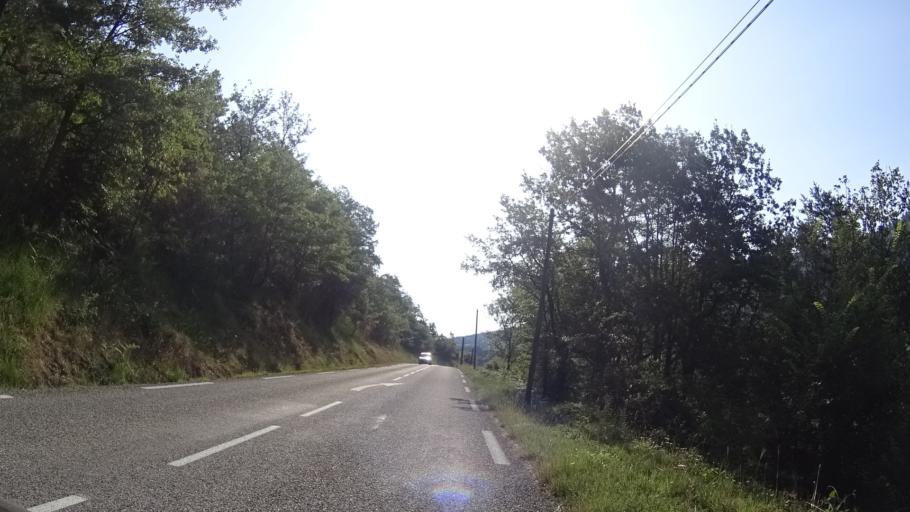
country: FR
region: Midi-Pyrenees
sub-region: Departement de l'Ariege
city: Belesta
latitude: 42.9112
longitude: 1.9699
